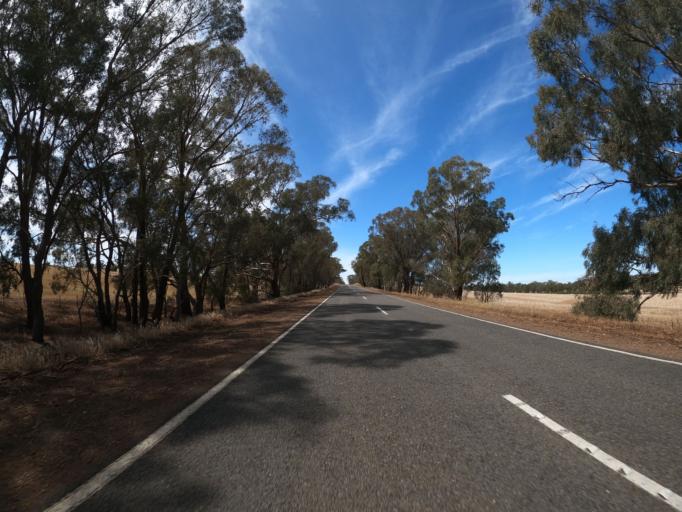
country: AU
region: Victoria
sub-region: Benalla
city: Benalla
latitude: -36.3463
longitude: 145.9608
